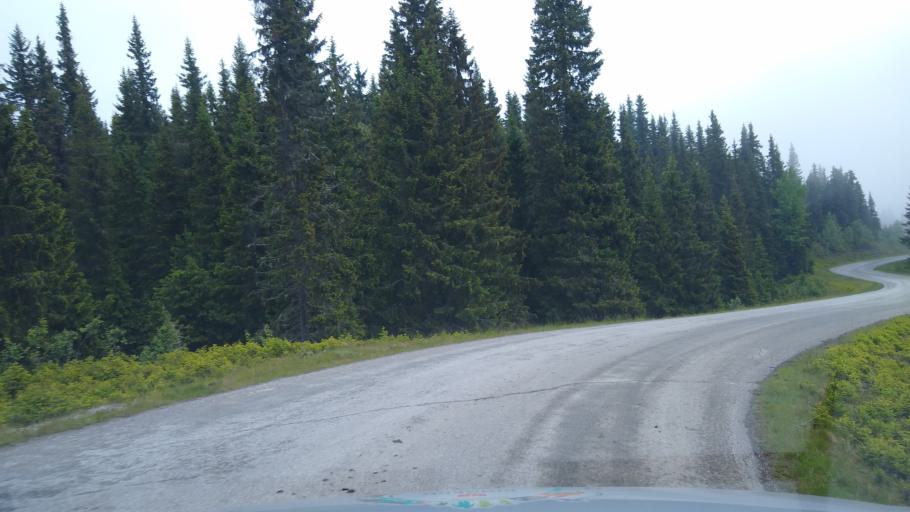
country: NO
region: Oppland
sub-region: Ringebu
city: Ringebu
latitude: 61.4931
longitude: 10.1188
